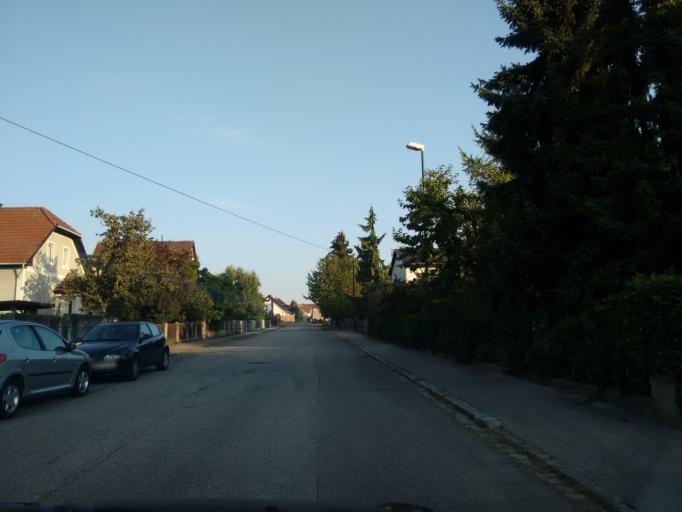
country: AT
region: Upper Austria
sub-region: Wels Stadt
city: Wels
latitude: 48.1696
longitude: 14.0157
